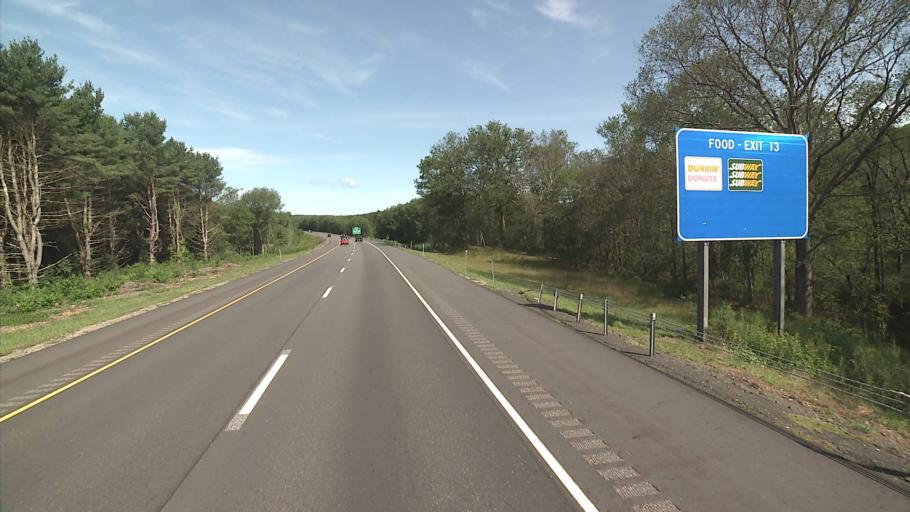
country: US
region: Connecticut
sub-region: Hartford County
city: Terramuggus
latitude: 41.6227
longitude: -72.4380
